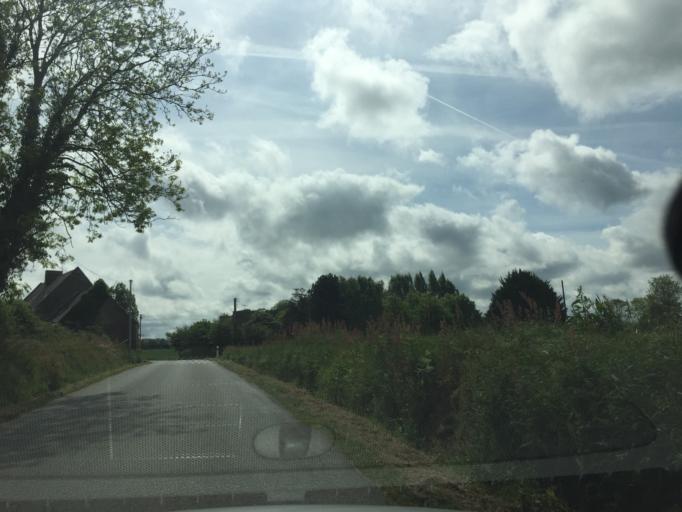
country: FR
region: Brittany
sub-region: Departement des Cotes-d'Armor
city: Corseul
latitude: 48.5270
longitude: -2.1653
